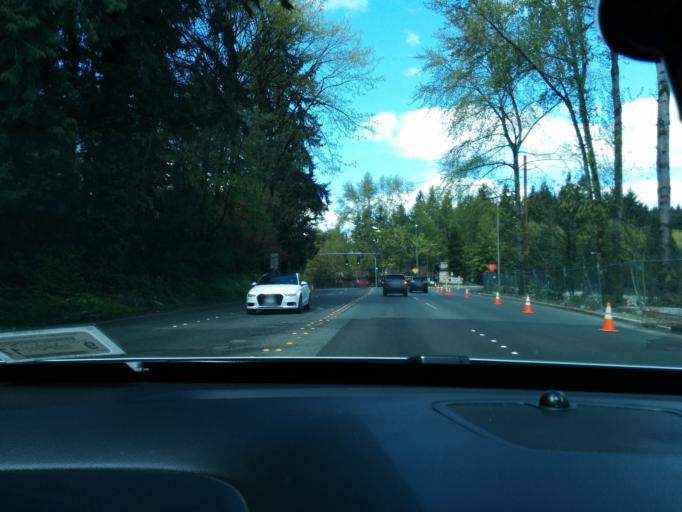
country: US
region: Washington
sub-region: King County
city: Bellevue
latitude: 47.5928
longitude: -122.1945
